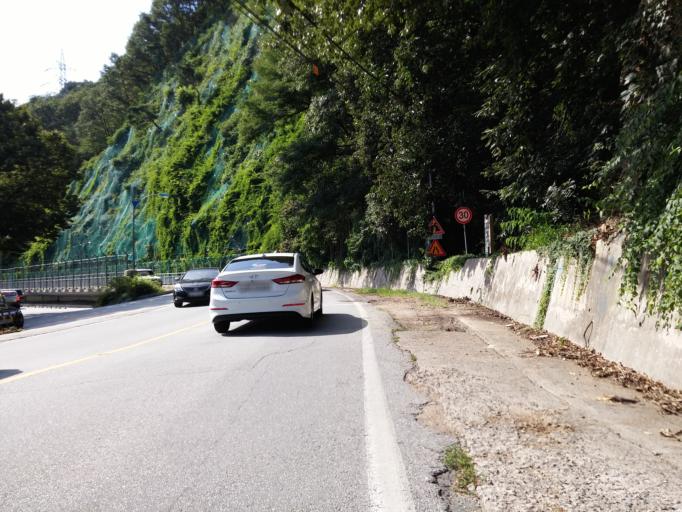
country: KR
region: Daejeon
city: Sintansin
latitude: 36.4799
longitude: 127.4814
